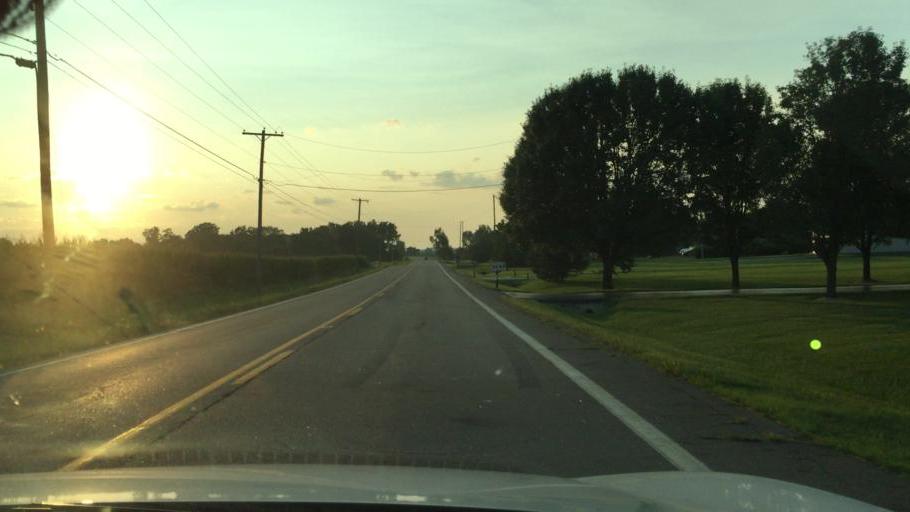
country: US
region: Ohio
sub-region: Madison County
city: Choctaw Lake
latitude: 39.9830
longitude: -83.3989
